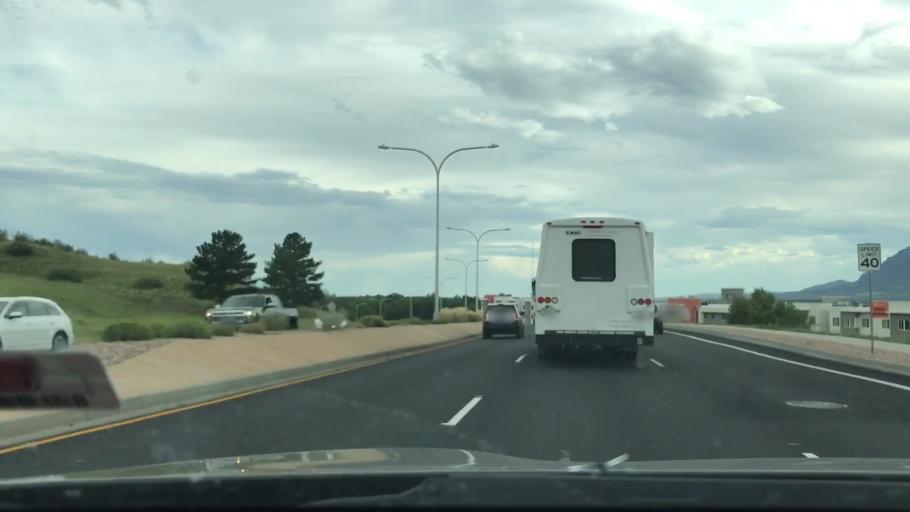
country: US
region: Colorado
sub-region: El Paso County
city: Colorado Springs
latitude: 38.8950
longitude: -104.8062
